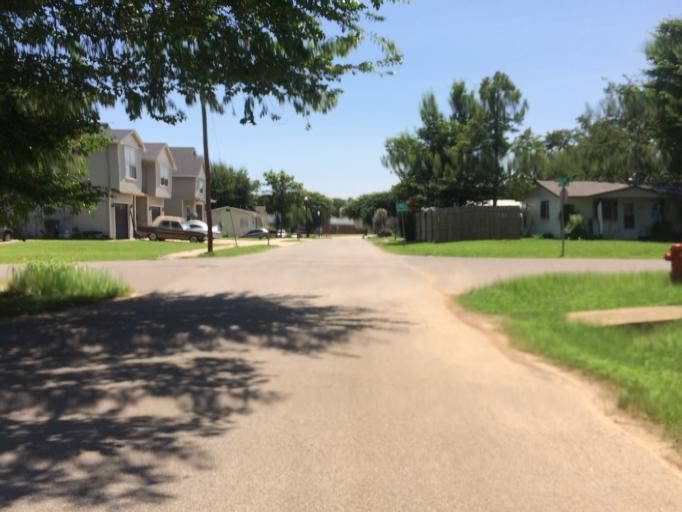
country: US
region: Oklahoma
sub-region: Cleveland County
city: Norman
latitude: 35.2198
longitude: -97.4356
